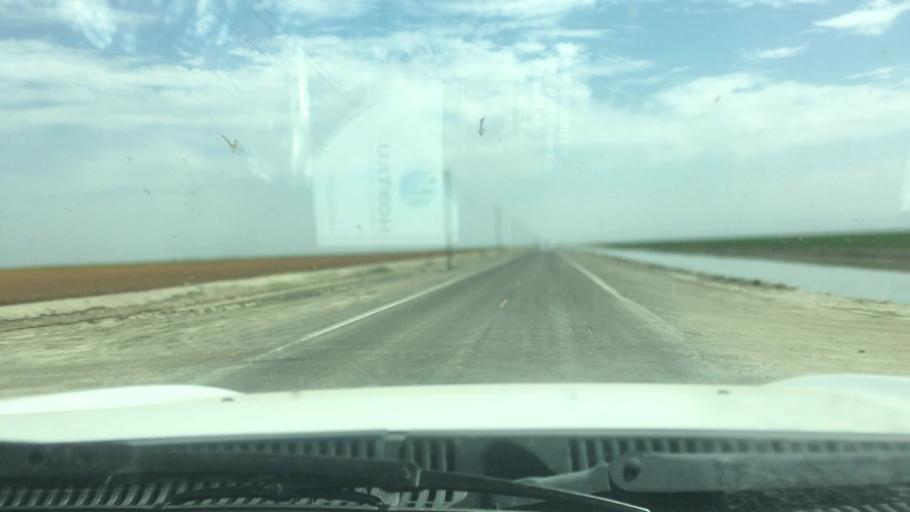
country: US
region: California
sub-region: Tulare County
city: Alpaugh
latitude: 35.9056
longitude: -119.5733
